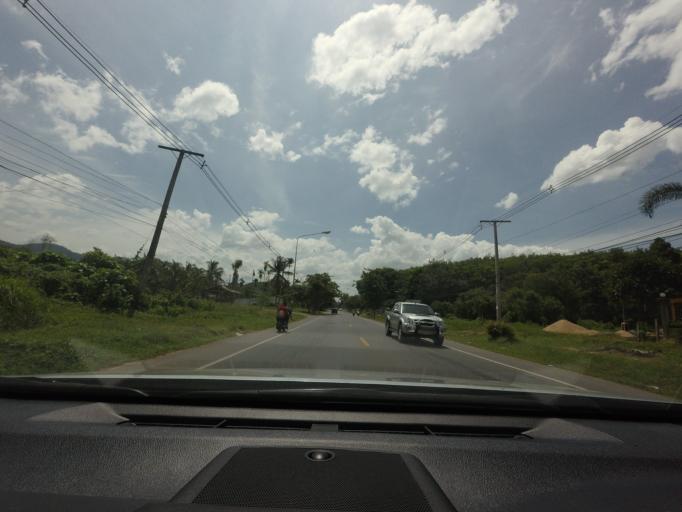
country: TH
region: Yala
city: Krong Pi Nang
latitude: 6.4637
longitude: 101.3291
